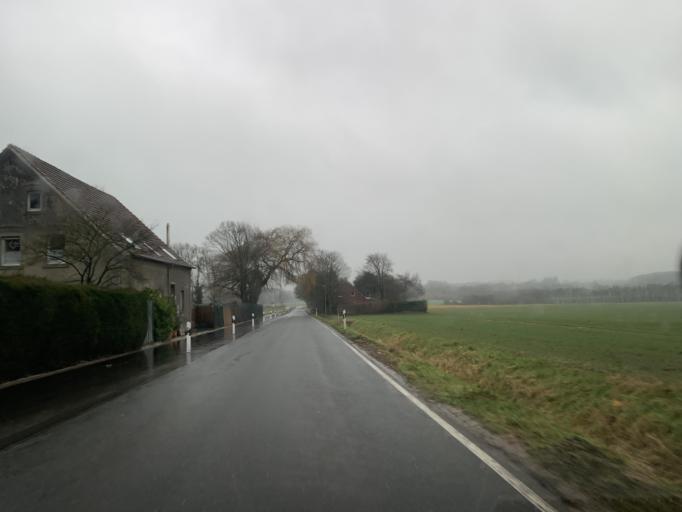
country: DE
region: North Rhine-Westphalia
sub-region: Regierungsbezirk Munster
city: Havixbeck
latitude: 51.9314
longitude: 7.4127
